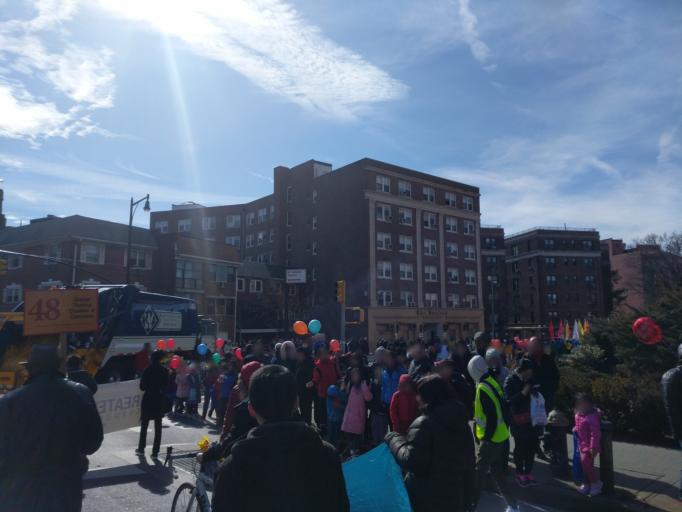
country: US
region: New York
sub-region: Queens County
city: Jamaica
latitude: 40.7579
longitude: -73.8253
